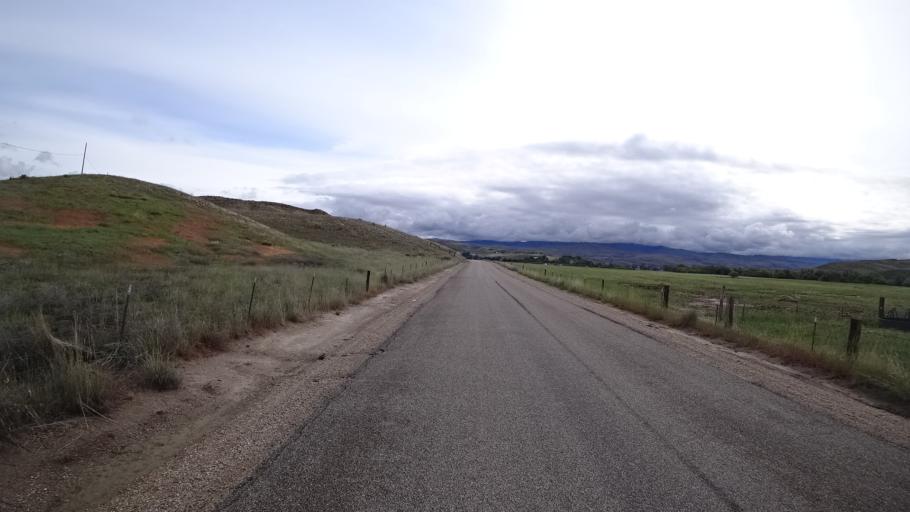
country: US
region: Idaho
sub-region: Ada County
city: Eagle
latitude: 43.7328
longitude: -116.3137
